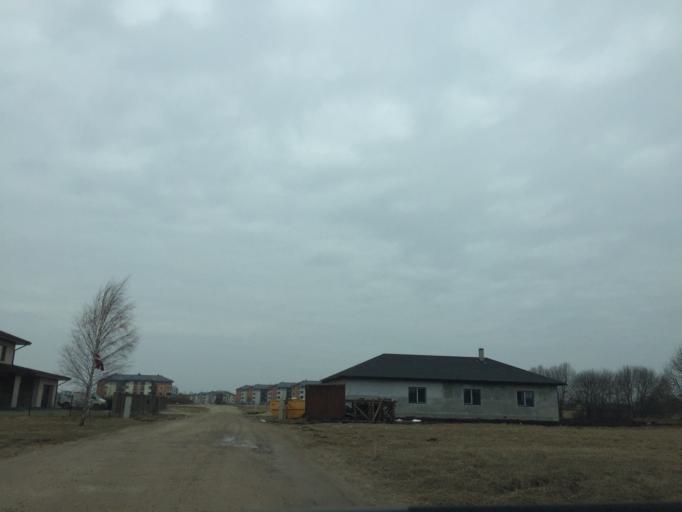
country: LV
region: Marupe
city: Marupe
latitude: 56.8818
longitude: 24.0550
